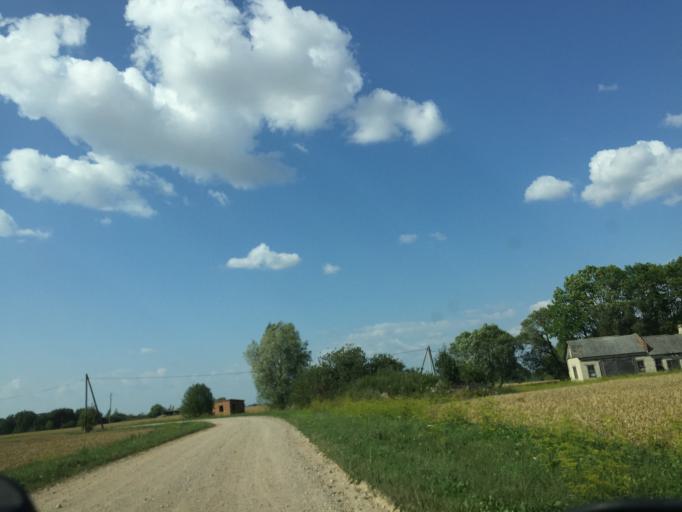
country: LV
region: Jelgava
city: Jelgava
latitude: 56.4482
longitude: 23.7497
